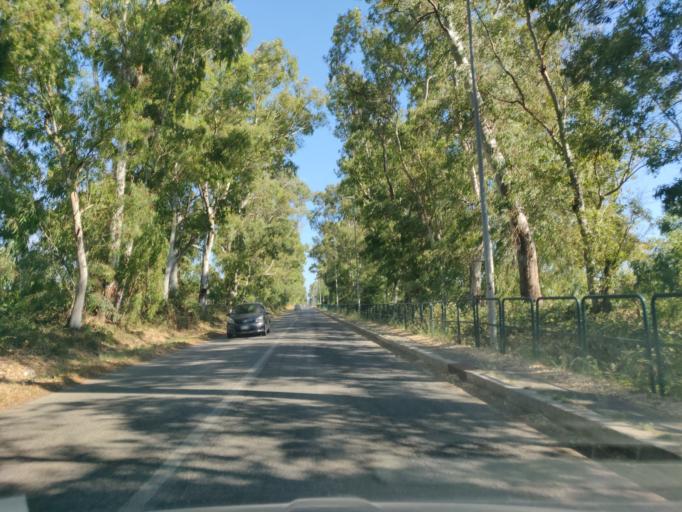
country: IT
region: Latium
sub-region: Citta metropolitana di Roma Capitale
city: Aurelia
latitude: 42.1427
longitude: 11.7645
